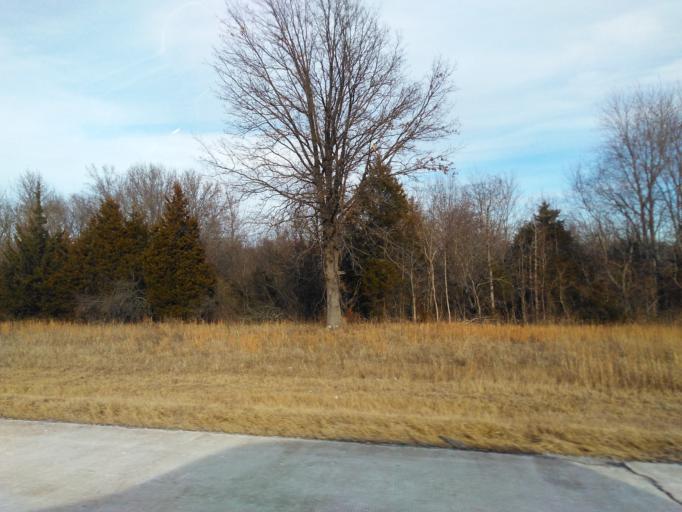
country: US
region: Illinois
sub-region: Jefferson County
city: Mount Vernon
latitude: 38.2799
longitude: -88.9376
